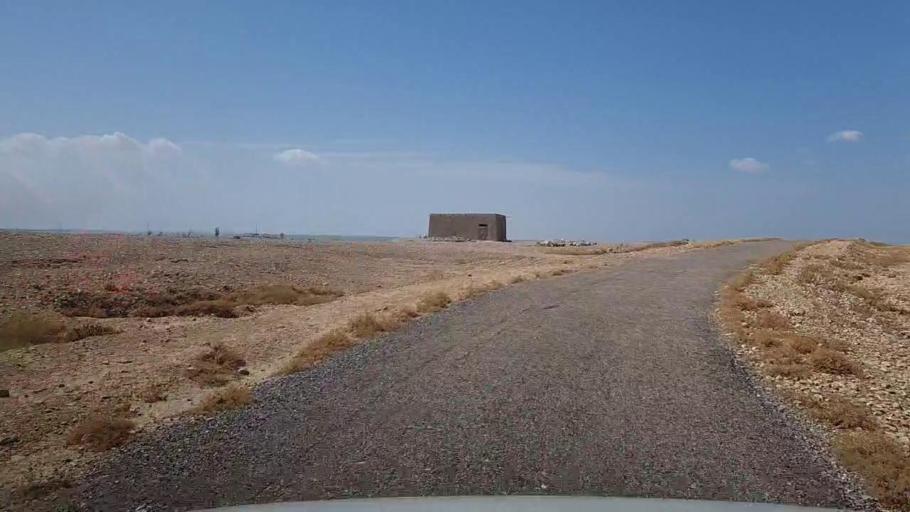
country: PK
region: Sindh
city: Bhan
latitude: 26.3819
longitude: 67.6292
